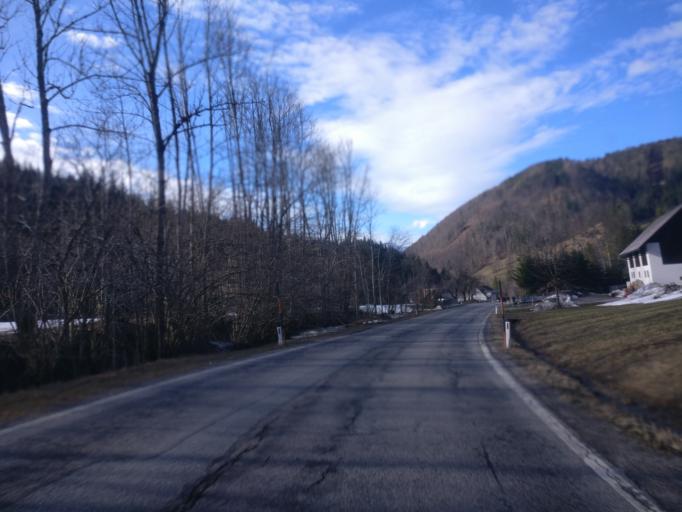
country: AT
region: Styria
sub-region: Politischer Bezirk Liezen
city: Sankt Gallen
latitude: 47.6709
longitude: 14.6447
